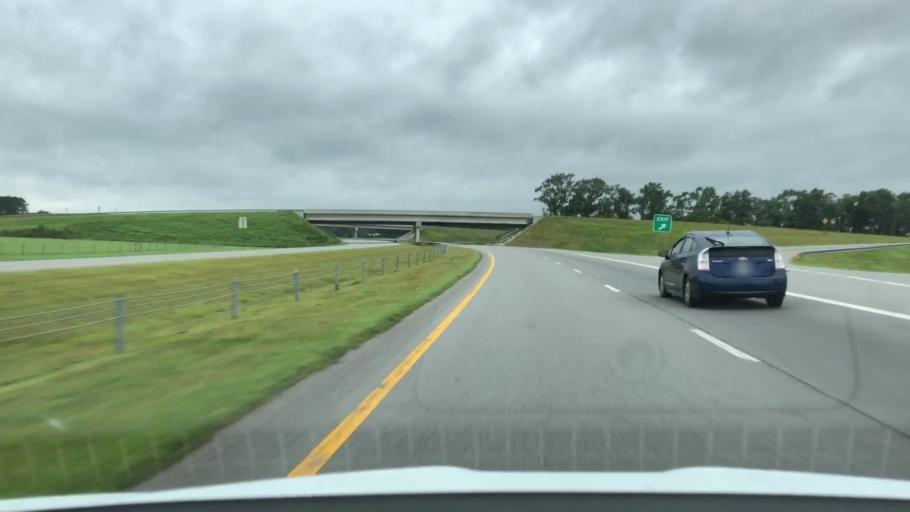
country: US
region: North Carolina
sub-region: Lenoir County
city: Kinston
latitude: 35.2646
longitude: -77.6715
